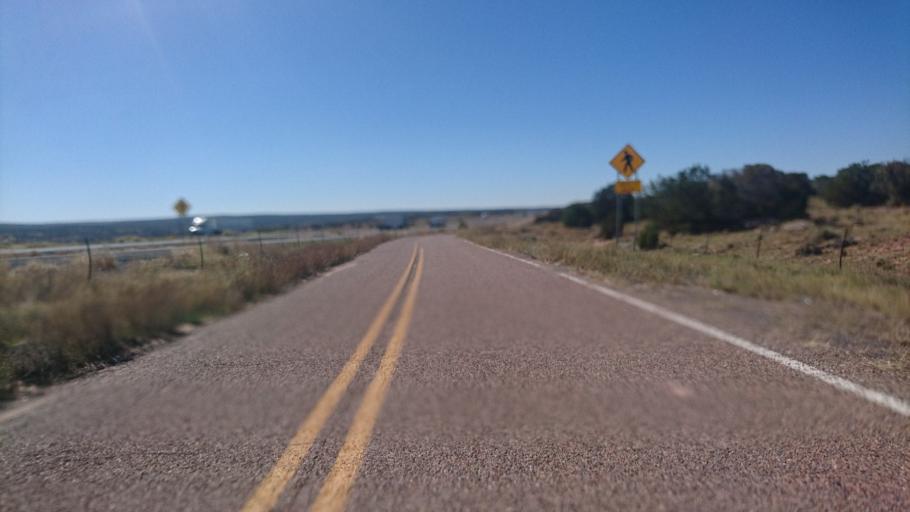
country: US
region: Arizona
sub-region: Apache County
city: Houck
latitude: 35.2883
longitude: -109.1598
